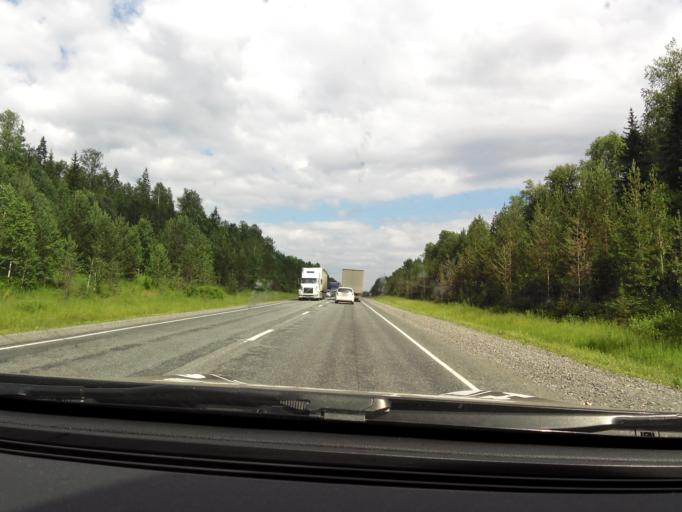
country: RU
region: Sverdlovsk
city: Nizhniye Sergi
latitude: 56.8248
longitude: 59.2728
